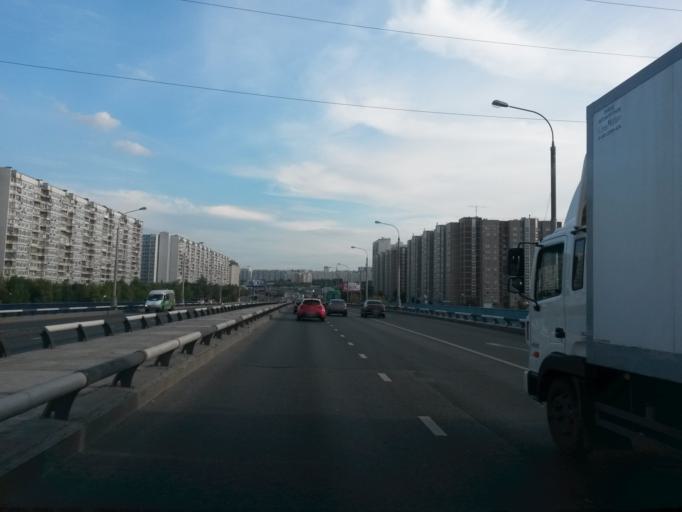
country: RU
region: Moscow
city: Brateyevo
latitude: 55.6389
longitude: 37.7481
